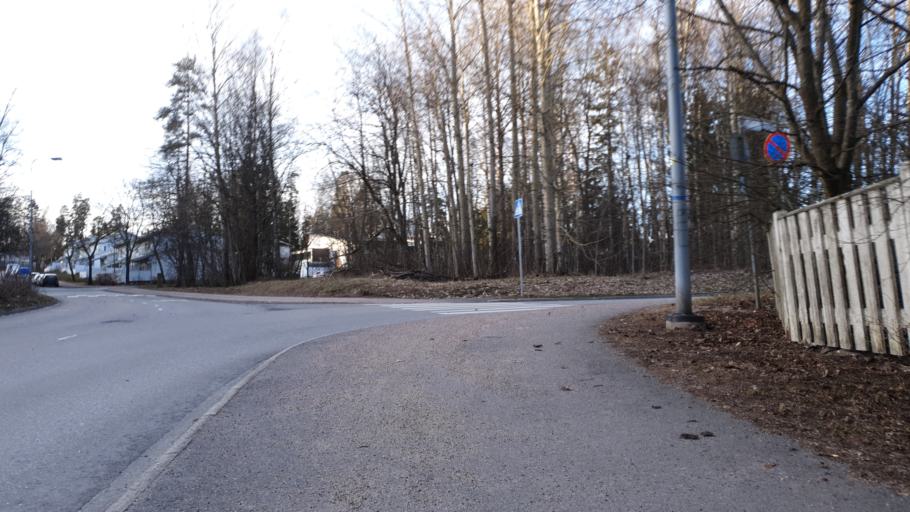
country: FI
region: Uusimaa
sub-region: Helsinki
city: Vantaa
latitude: 60.3082
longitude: 25.0042
